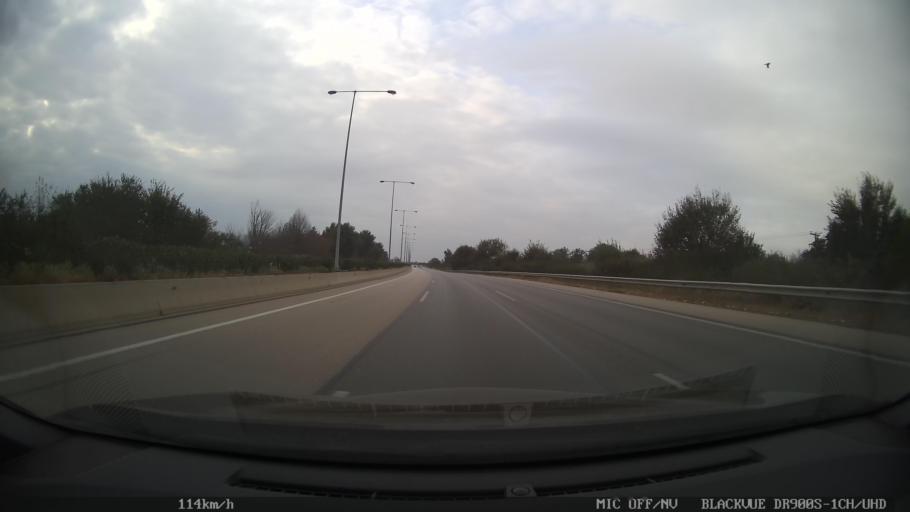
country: GR
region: Central Macedonia
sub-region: Nomos Thessalonikis
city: Nea Magnisia
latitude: 40.6842
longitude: 22.8326
